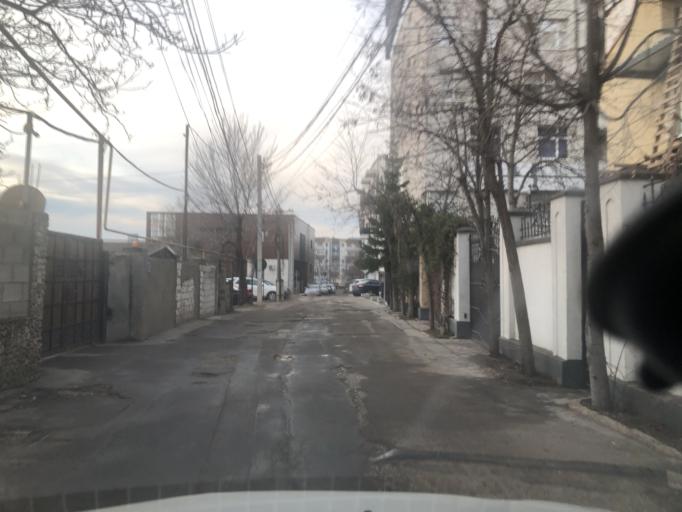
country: MD
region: Chisinau
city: Chisinau
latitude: 47.0425
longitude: 28.8559
